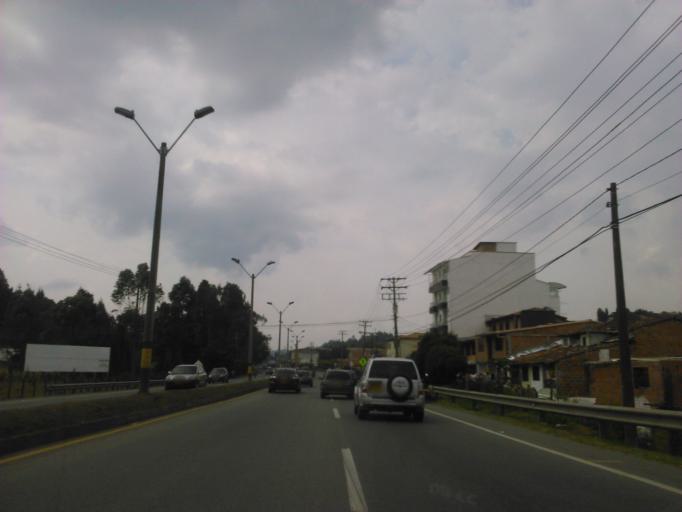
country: CO
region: Antioquia
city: Guarne
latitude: 6.2703
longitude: -75.4380
